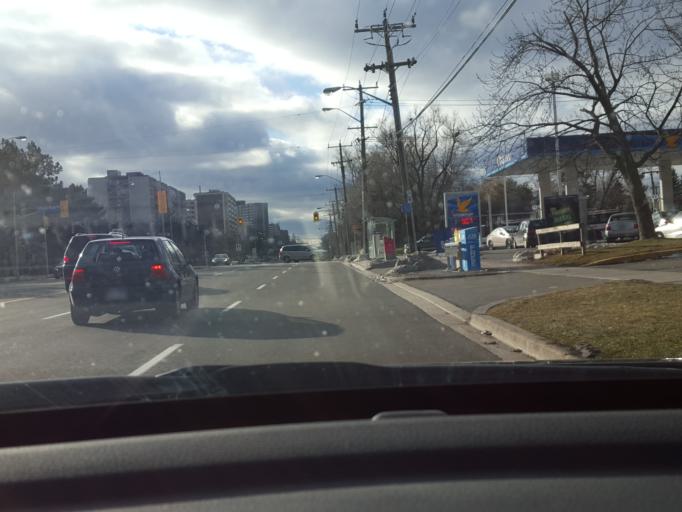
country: CA
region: Ontario
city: Scarborough
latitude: 43.7644
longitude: -79.2047
